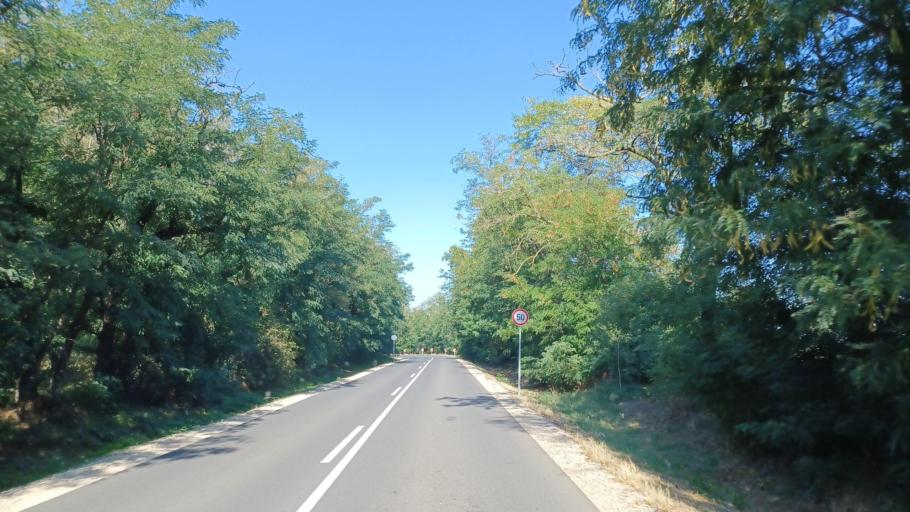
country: HU
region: Fejer
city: Cece
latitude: 46.7583
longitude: 18.6611
